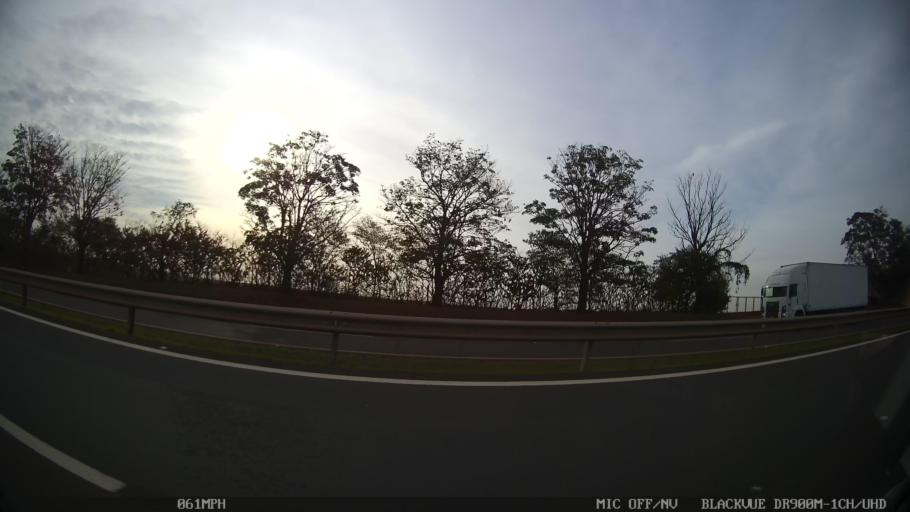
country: BR
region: Sao Paulo
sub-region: Iracemapolis
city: Iracemapolis
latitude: -22.6704
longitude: -47.5539
